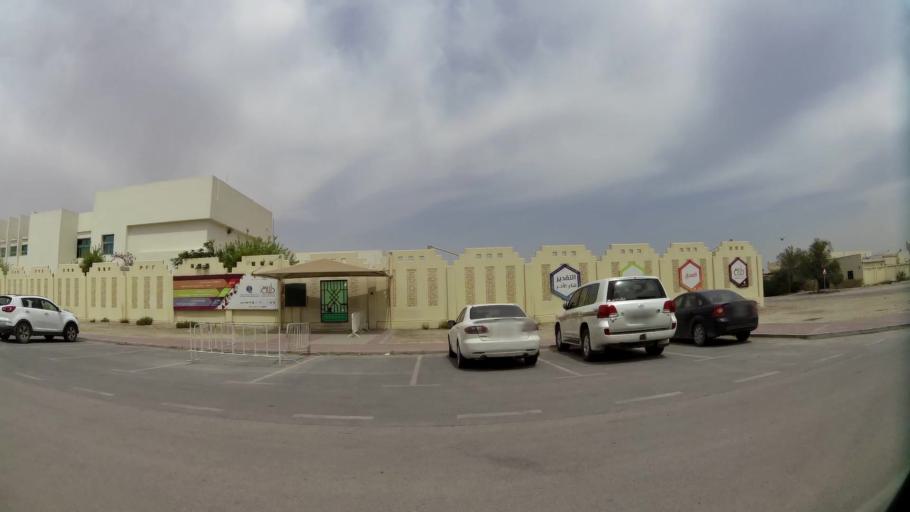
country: QA
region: Baladiyat ar Rayyan
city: Ar Rayyan
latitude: 25.2789
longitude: 51.4602
